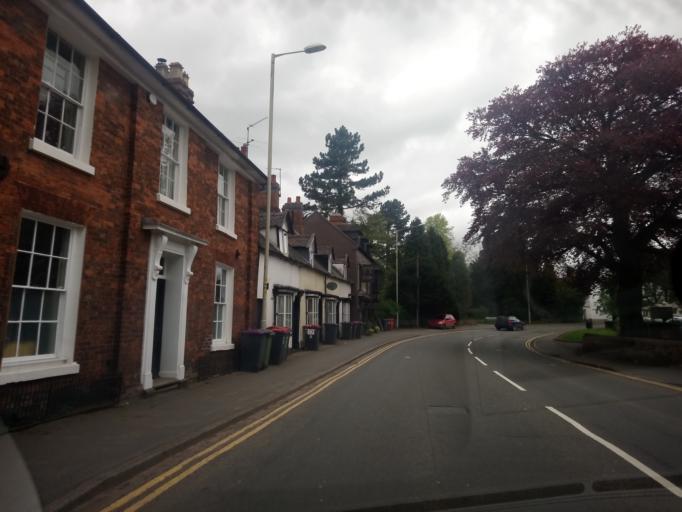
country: GB
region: England
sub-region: Telford and Wrekin
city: Newport
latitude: 52.7715
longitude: -2.3820
